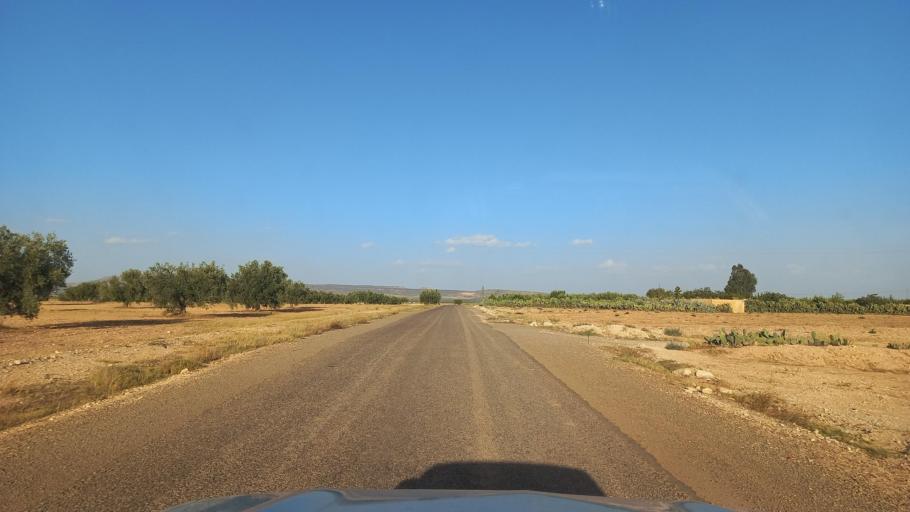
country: TN
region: Al Qasrayn
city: Kasserine
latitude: 35.2870
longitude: 9.0340
